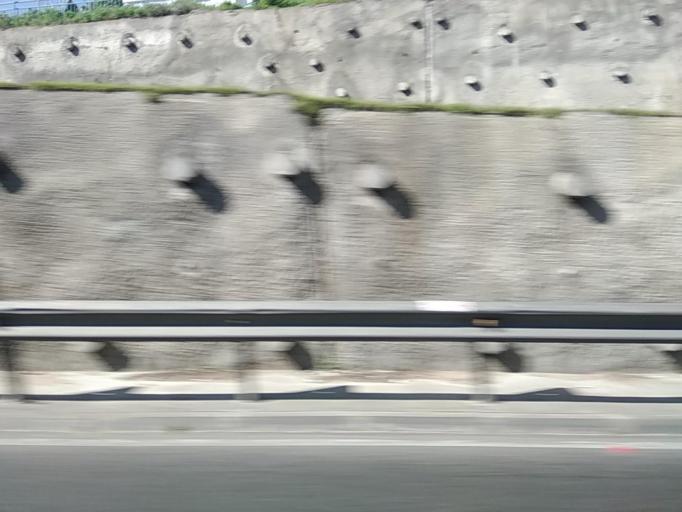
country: CL
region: Valparaiso
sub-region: Provincia de Valparaiso
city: Vina del Mar
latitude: -33.0198
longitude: -71.5019
